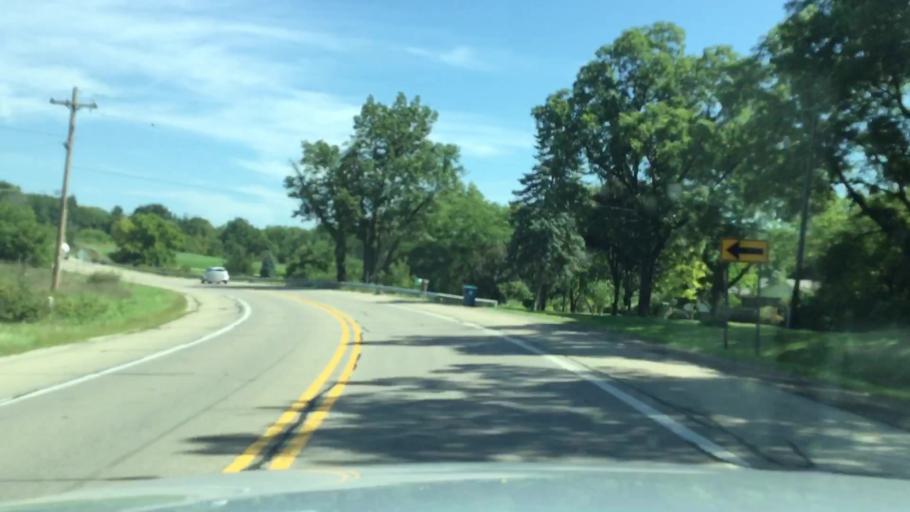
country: US
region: Michigan
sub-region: Washtenaw County
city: Manchester
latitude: 42.0678
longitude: -84.0979
